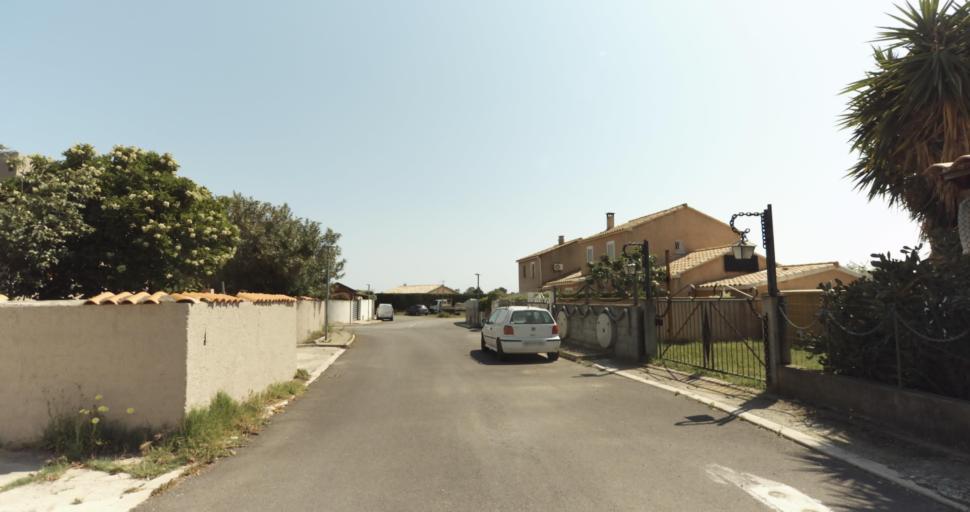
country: FR
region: Corsica
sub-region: Departement de la Haute-Corse
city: Biguglia
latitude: 42.6143
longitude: 9.4291
